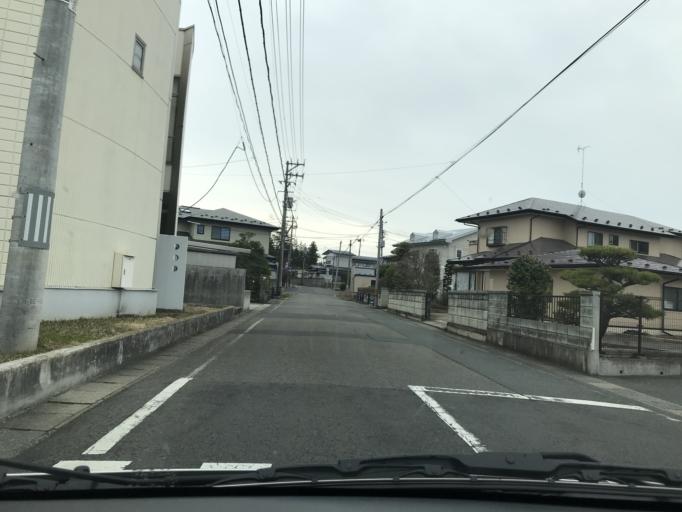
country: JP
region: Iwate
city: Mizusawa
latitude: 39.1372
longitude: 141.1326
